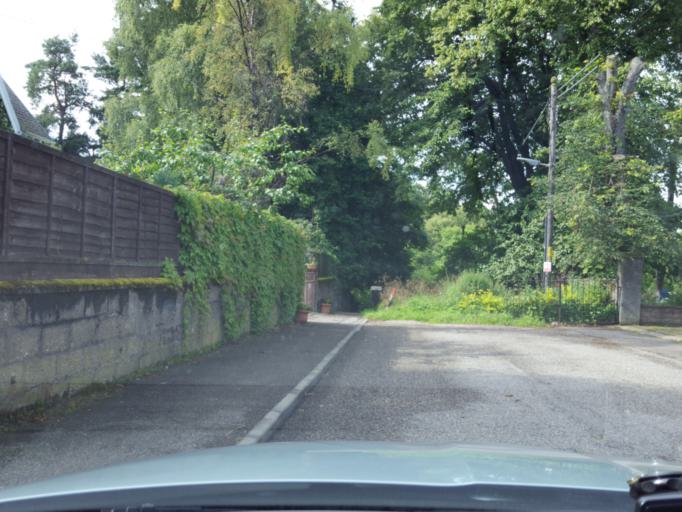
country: GB
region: Scotland
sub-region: Moray
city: Rothes
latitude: 57.4687
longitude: -3.2273
